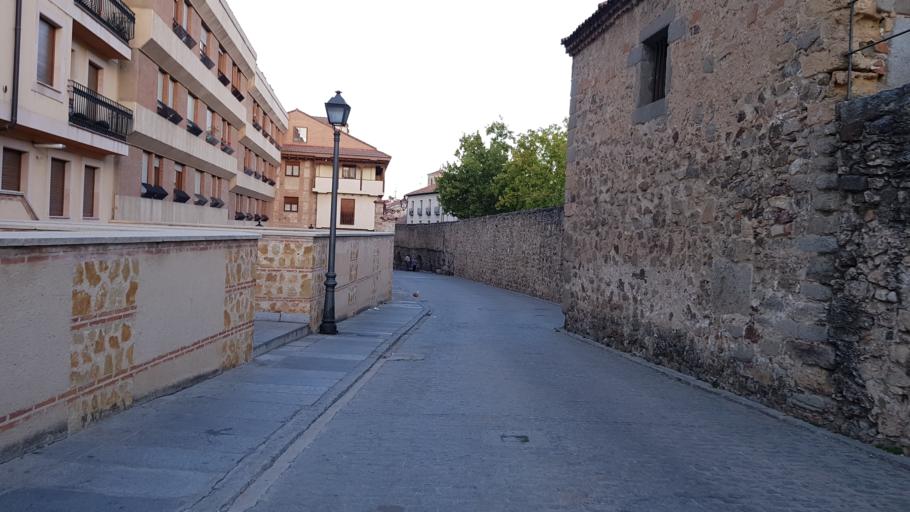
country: ES
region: Castille and Leon
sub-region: Provincia de Segovia
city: Segovia
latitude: 40.9453
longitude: -4.1114
